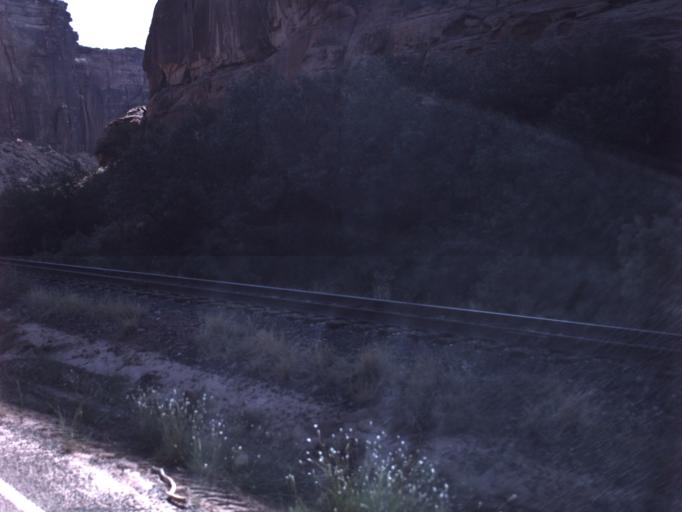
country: US
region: Utah
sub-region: Grand County
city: Moab
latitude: 38.5498
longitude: -109.6476
